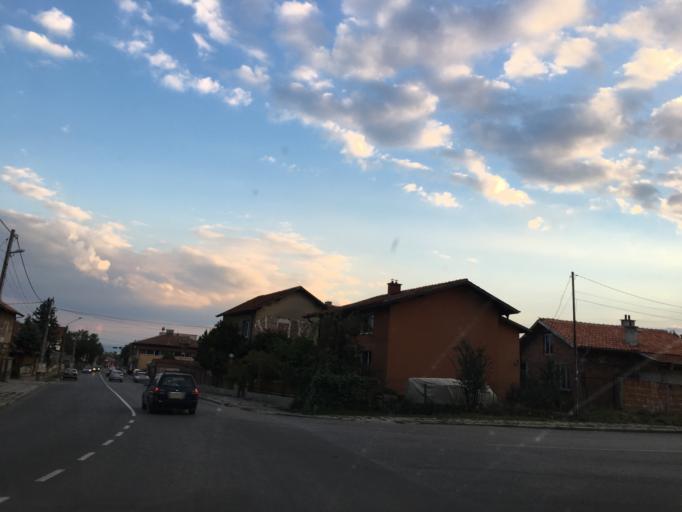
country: BG
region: Sofia-Capital
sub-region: Stolichna Obshtina
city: Sofia
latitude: 42.8270
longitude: 23.3538
